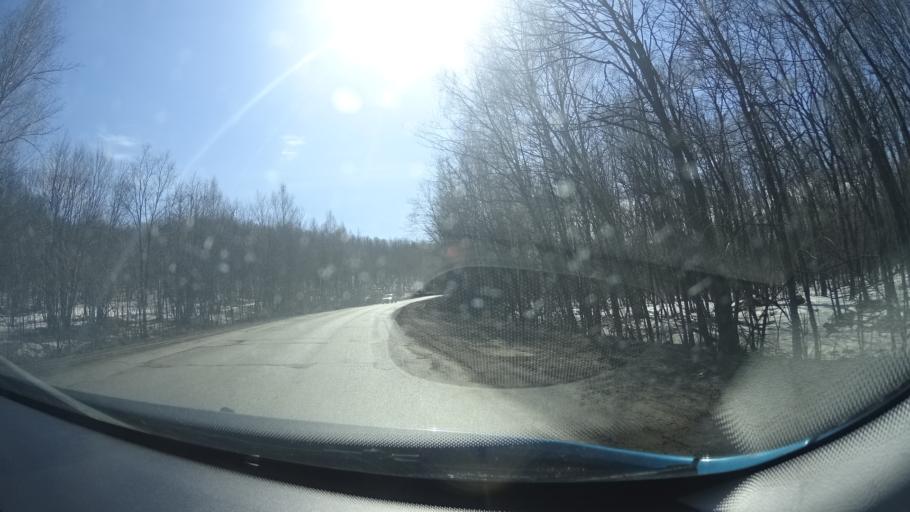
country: RU
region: Bashkortostan
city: Oktyabr'skiy
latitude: 54.4744
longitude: 53.5784
